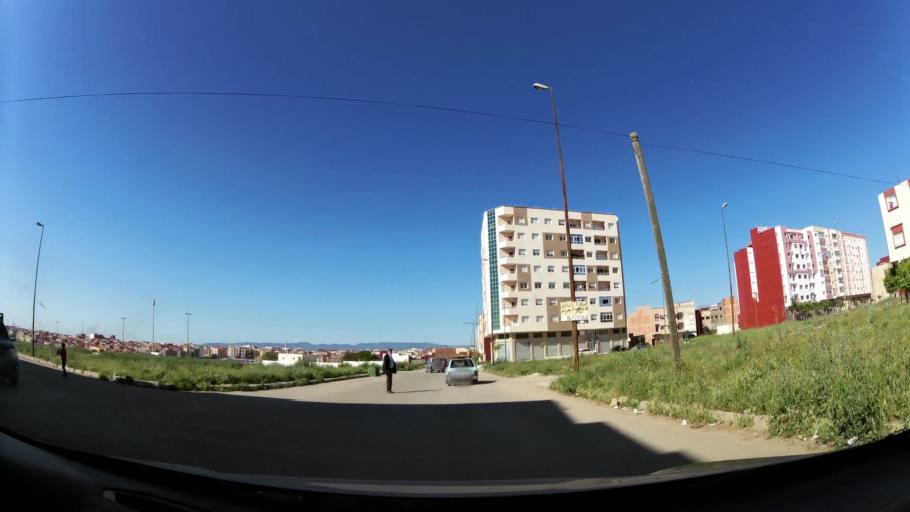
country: MA
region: Meknes-Tafilalet
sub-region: Meknes
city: Meknes
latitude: 33.8797
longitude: -5.5807
